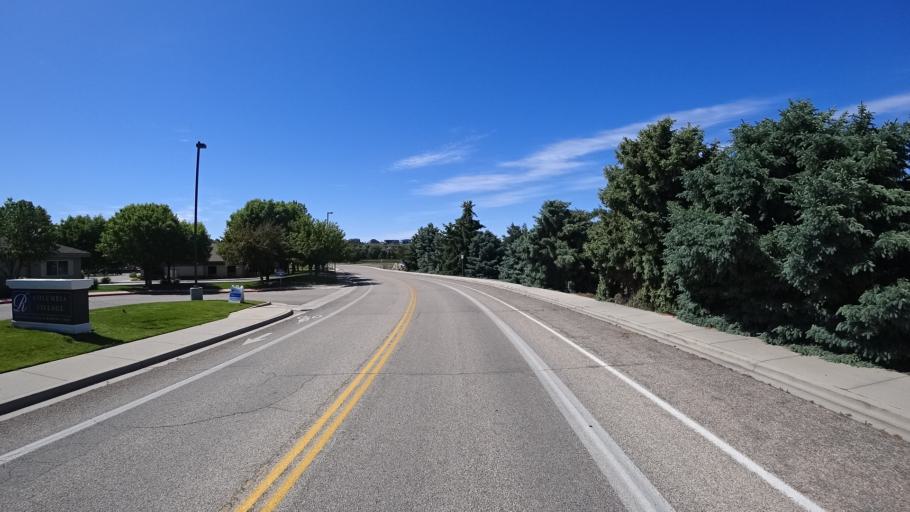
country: US
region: Idaho
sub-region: Ada County
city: Boise
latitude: 43.5486
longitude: -116.1413
